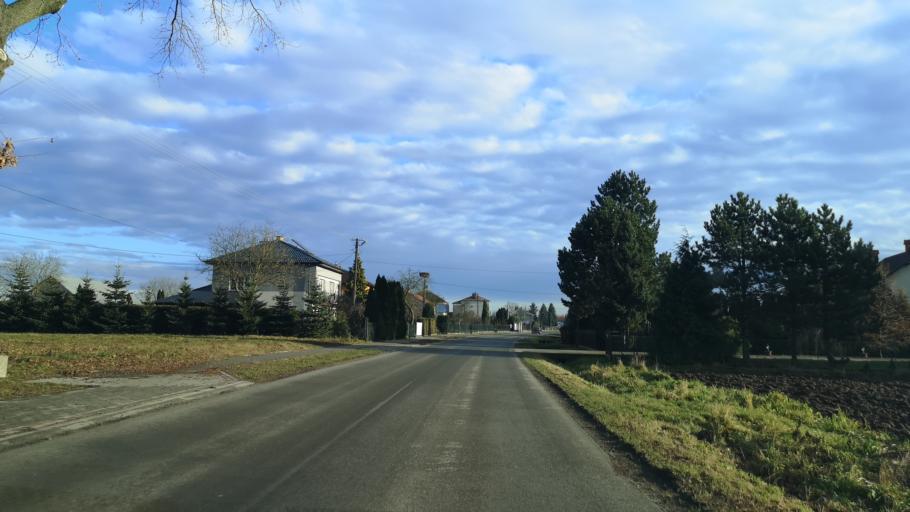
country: PL
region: Subcarpathian Voivodeship
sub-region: Powiat lezajski
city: Piskorowice
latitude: 50.2431
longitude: 22.5140
